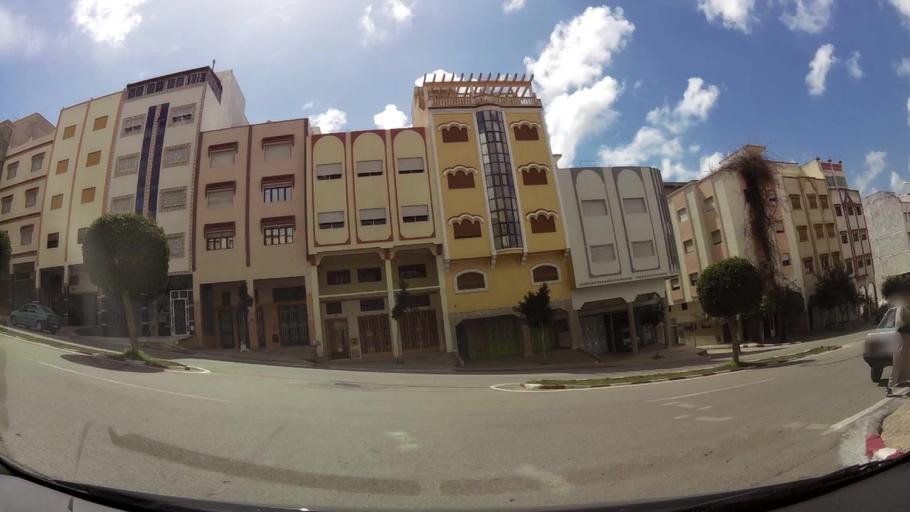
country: MA
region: Tanger-Tetouan
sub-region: Tanger-Assilah
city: Tangier
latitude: 35.7512
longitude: -5.8306
